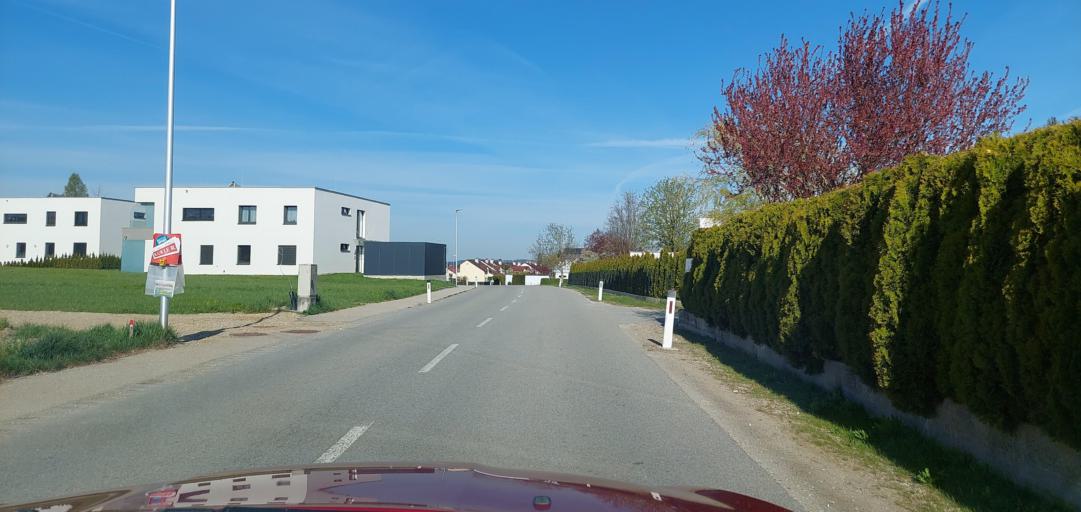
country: AT
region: Upper Austria
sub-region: Politischer Bezirk Ried im Innkreis
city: Ried im Innkreis
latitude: 48.2021
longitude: 13.5066
